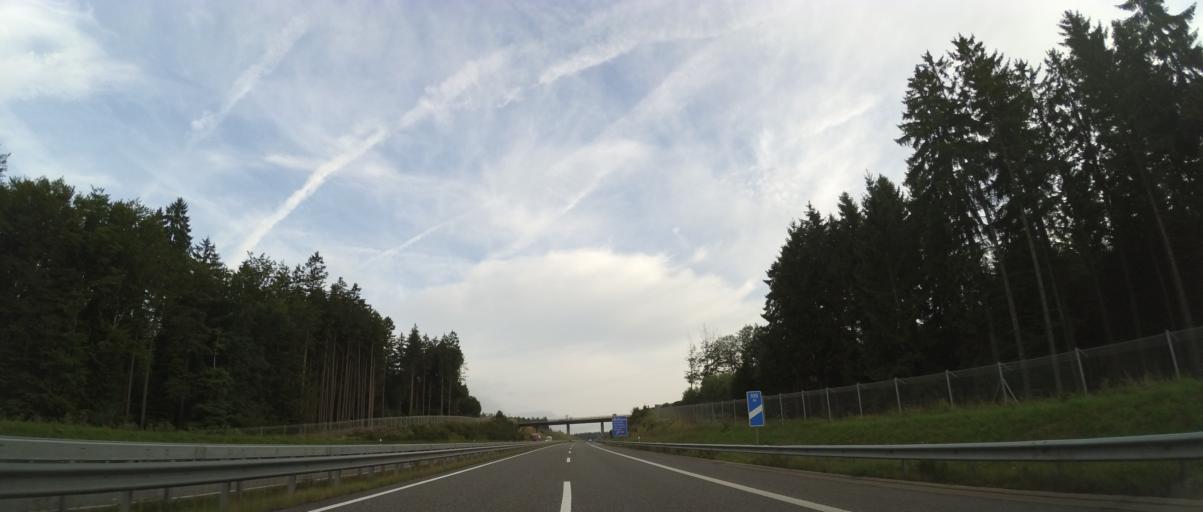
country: DE
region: Rheinland-Pfalz
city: Kradenbach
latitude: 50.2479
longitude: 6.8296
